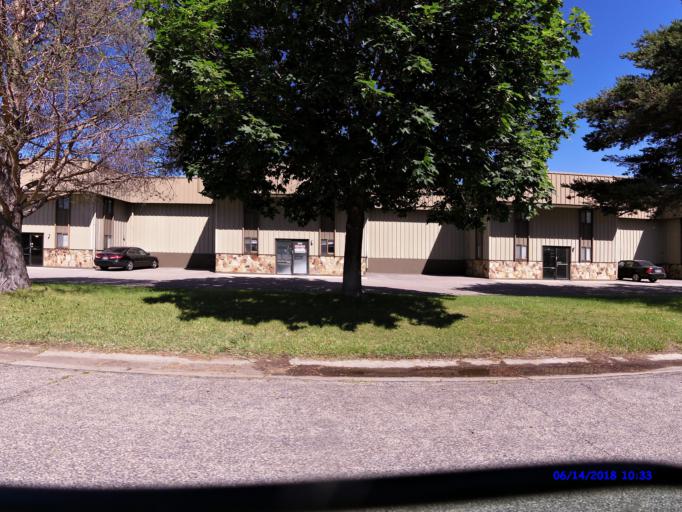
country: US
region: Utah
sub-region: Weber County
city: Marriott-Slaterville
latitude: 41.2167
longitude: -112.0133
